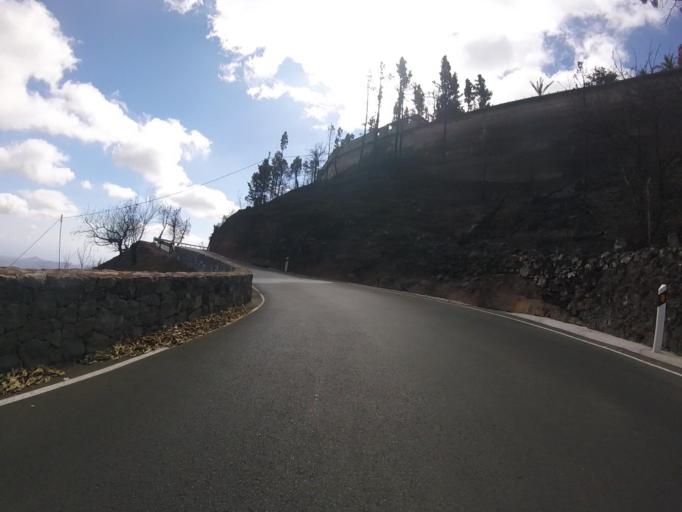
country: ES
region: Canary Islands
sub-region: Provincia de Las Palmas
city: Tejeda
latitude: 28.0034
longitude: -15.5960
